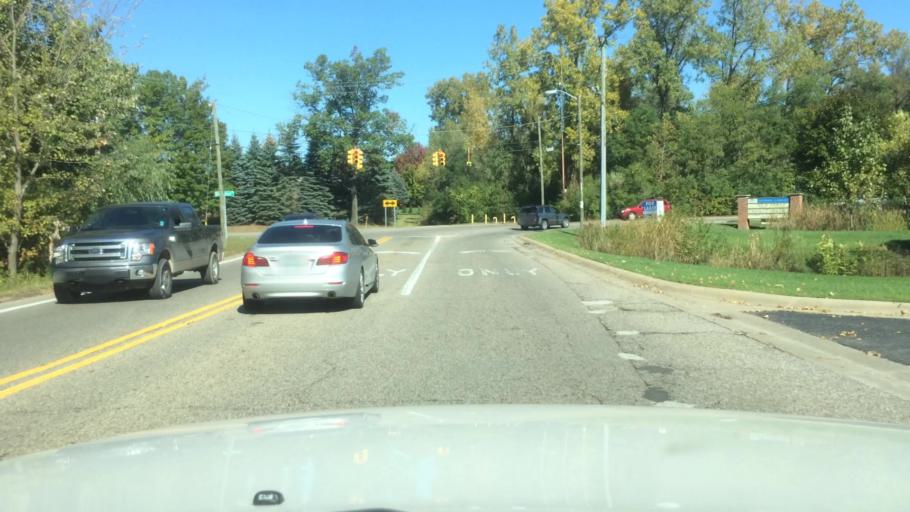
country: US
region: Michigan
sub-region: Oakland County
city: Wolverine Lake
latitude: 42.5772
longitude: -83.4502
